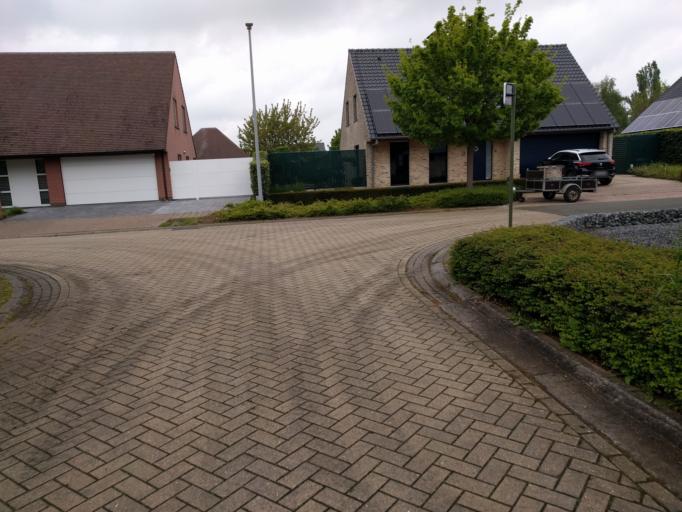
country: BE
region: Flanders
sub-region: Provincie West-Vlaanderen
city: Wevelgem
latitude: 50.8322
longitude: 3.2057
